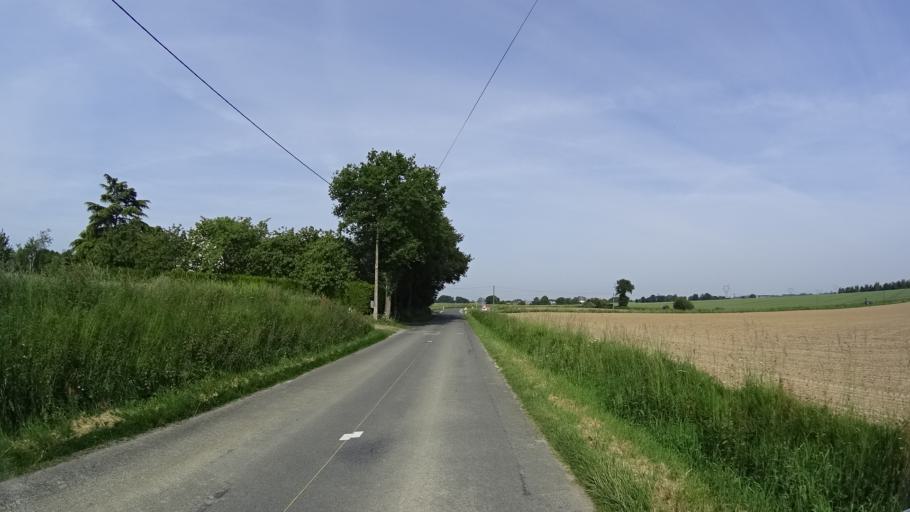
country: FR
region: Brittany
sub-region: Departement d'Ille-et-Vilaine
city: Chateaugiron
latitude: 48.0362
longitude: -1.5237
